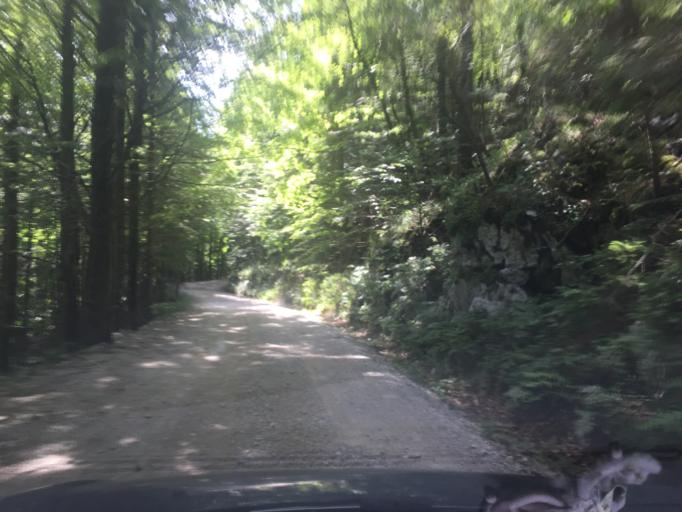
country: SI
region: Ajdovscina
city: Lokavec
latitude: 45.9871
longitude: 13.8380
